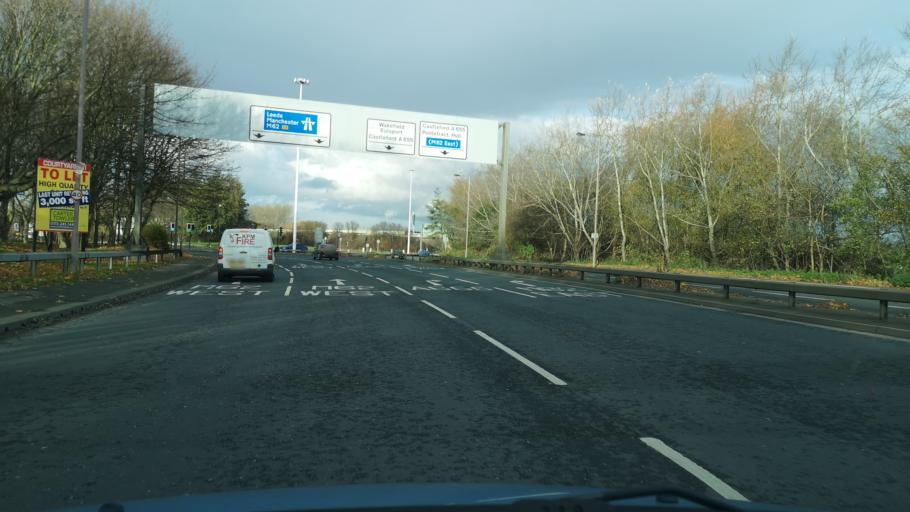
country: GB
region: England
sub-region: City and Borough of Wakefield
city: Normanton
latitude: 53.7065
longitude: -1.3969
